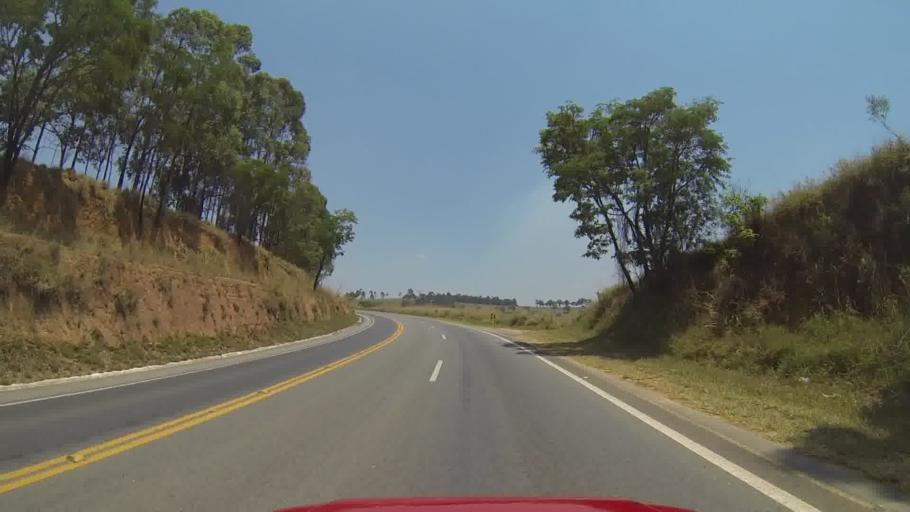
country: BR
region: Minas Gerais
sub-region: Itapecerica
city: Itapecerica
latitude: -20.3396
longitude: -45.2425
